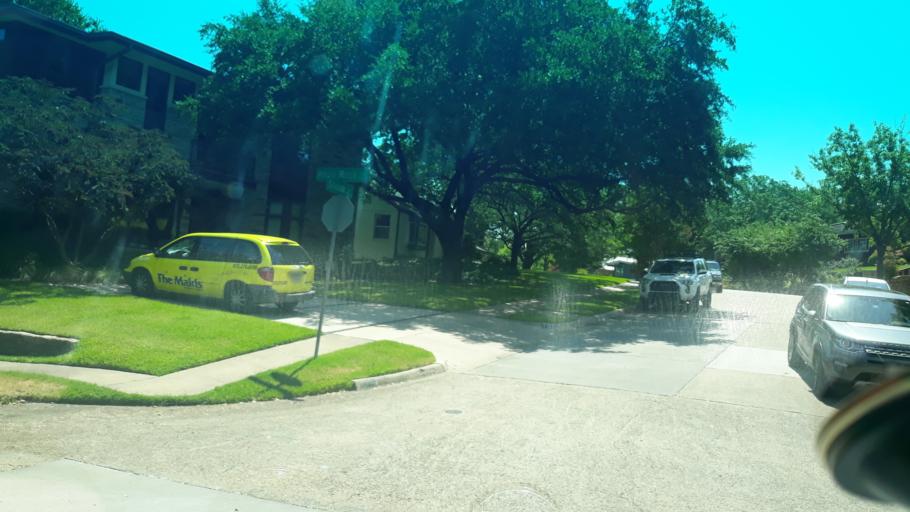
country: US
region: Texas
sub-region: Dallas County
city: Highland Park
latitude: 32.8160
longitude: -96.7366
